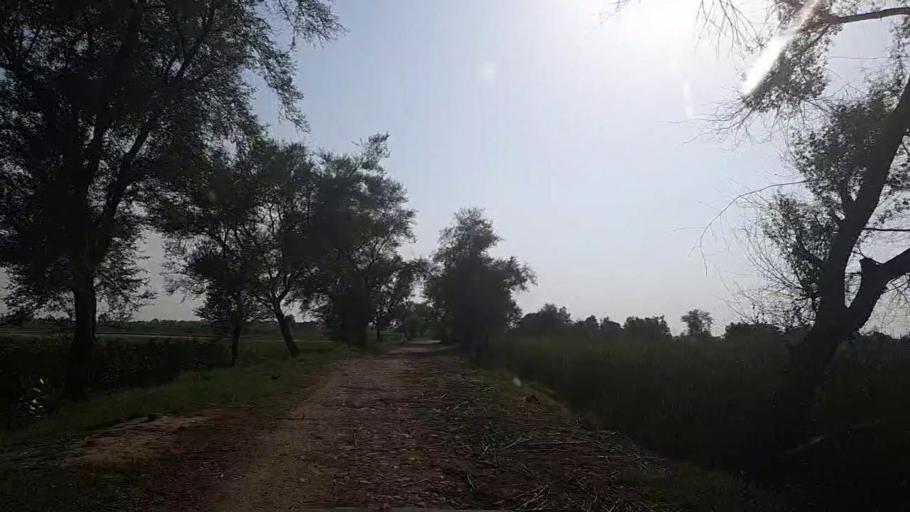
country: PK
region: Sindh
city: Khanpur
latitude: 27.7056
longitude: 69.3361
